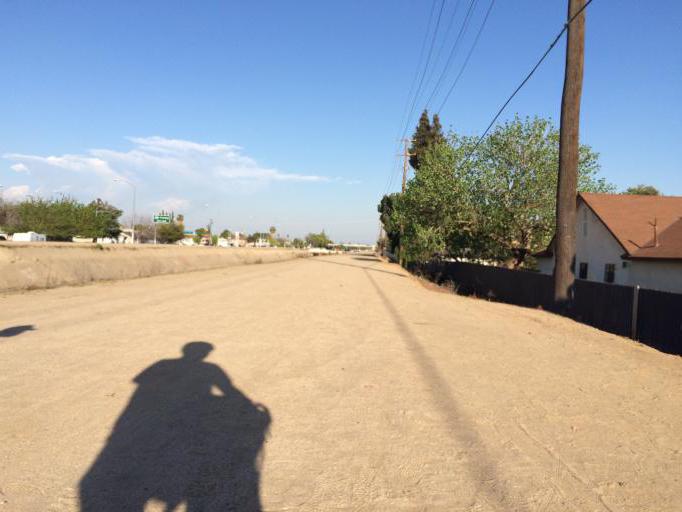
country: US
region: California
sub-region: Fresno County
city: Fresno
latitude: 36.7647
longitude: -119.7574
